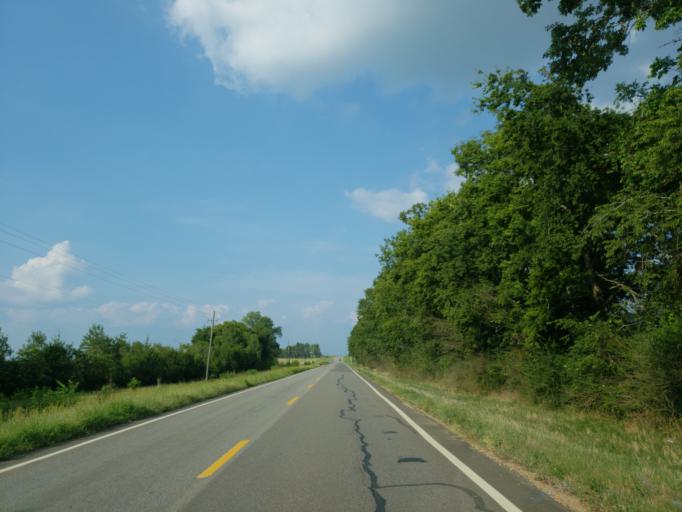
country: US
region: Alabama
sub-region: Greene County
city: Eutaw
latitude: 32.8010
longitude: -87.9602
